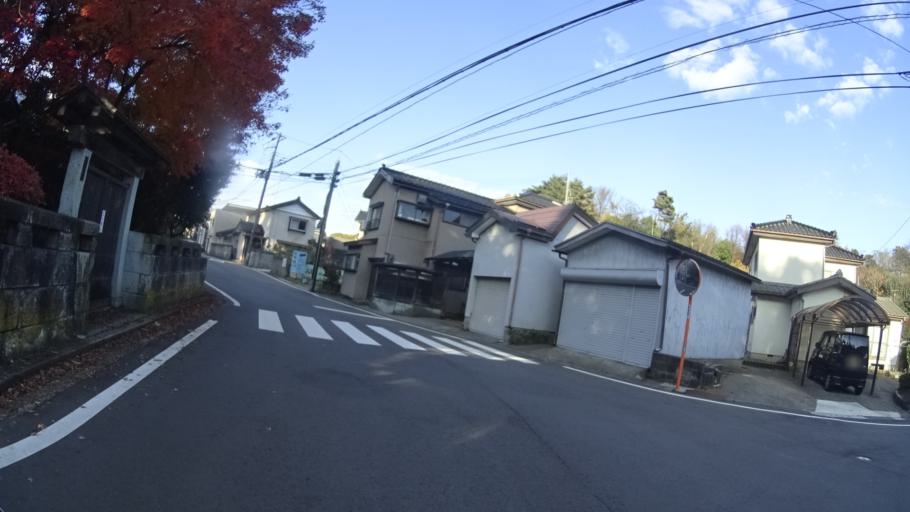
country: JP
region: Niigata
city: Kashiwazaki
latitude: 37.3598
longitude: 138.5457
